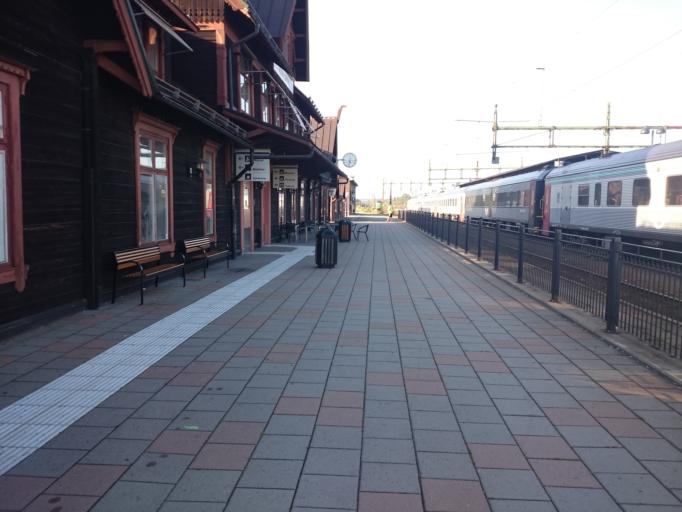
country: SE
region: Norrbotten
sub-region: Bodens Kommun
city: Boden
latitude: 65.8287
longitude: 21.7077
